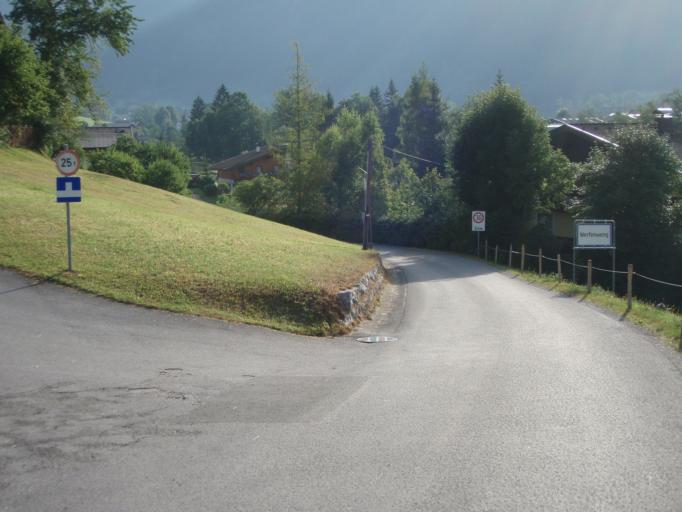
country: AT
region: Salzburg
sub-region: Politischer Bezirk Sankt Johann im Pongau
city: Werfenweng
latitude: 47.4617
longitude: 13.2491
